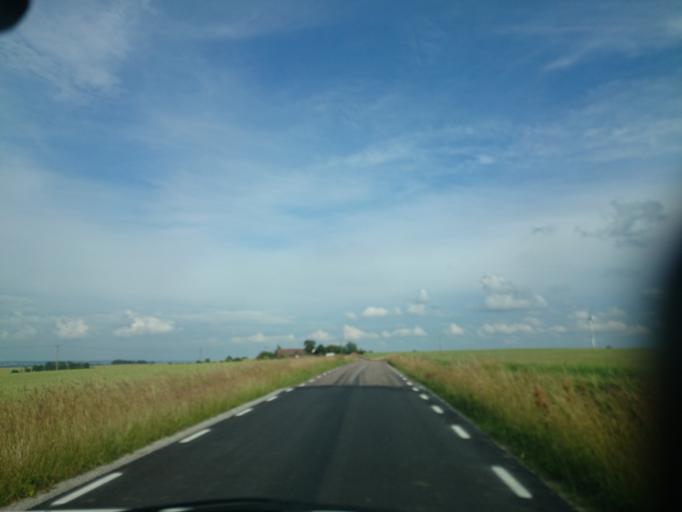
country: SE
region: Skane
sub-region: Lunds Kommun
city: Lund
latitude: 55.7490
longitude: 13.2520
